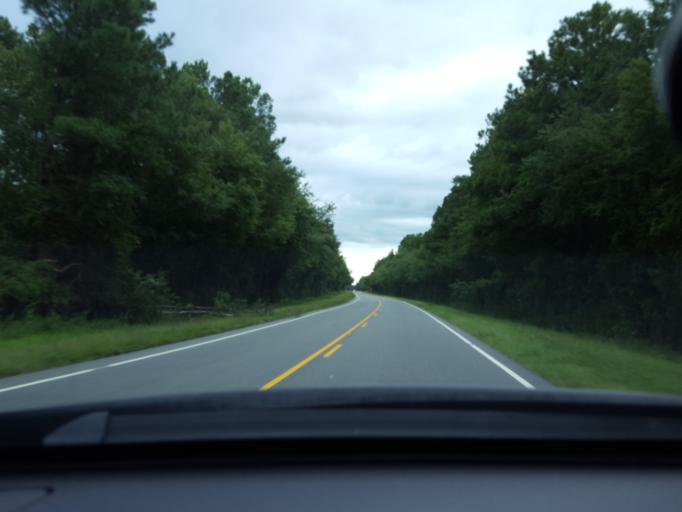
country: US
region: North Carolina
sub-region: Bladen County
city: Elizabethtown
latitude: 34.7005
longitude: -78.4767
